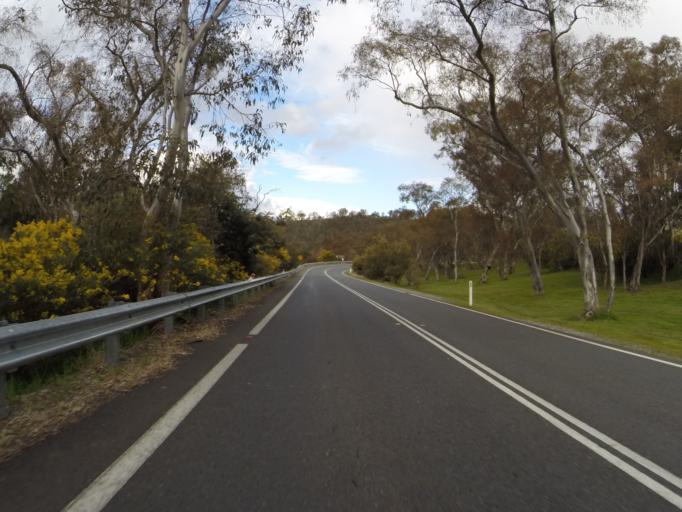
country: AU
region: Australian Capital Territory
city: Macquarie
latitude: -35.3204
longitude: 148.9541
